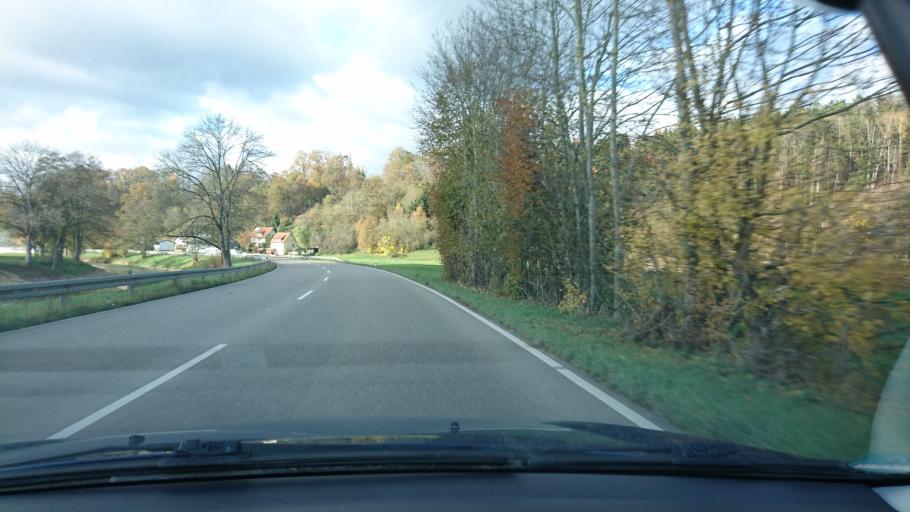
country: DE
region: Baden-Wuerttemberg
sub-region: Regierungsbezirk Stuttgart
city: Abtsgmund
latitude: 48.8973
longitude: 10.0057
